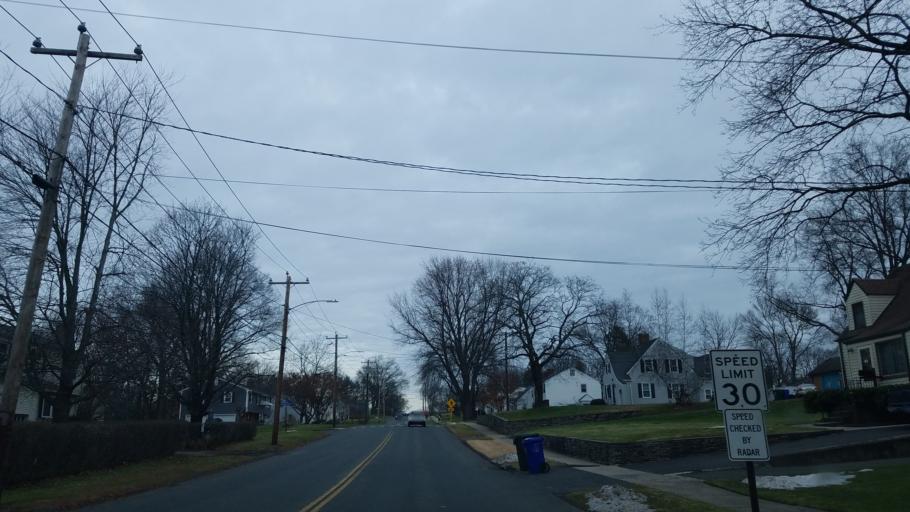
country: US
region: Connecticut
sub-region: Hartford County
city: Newington
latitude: 41.7116
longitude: -72.7351
